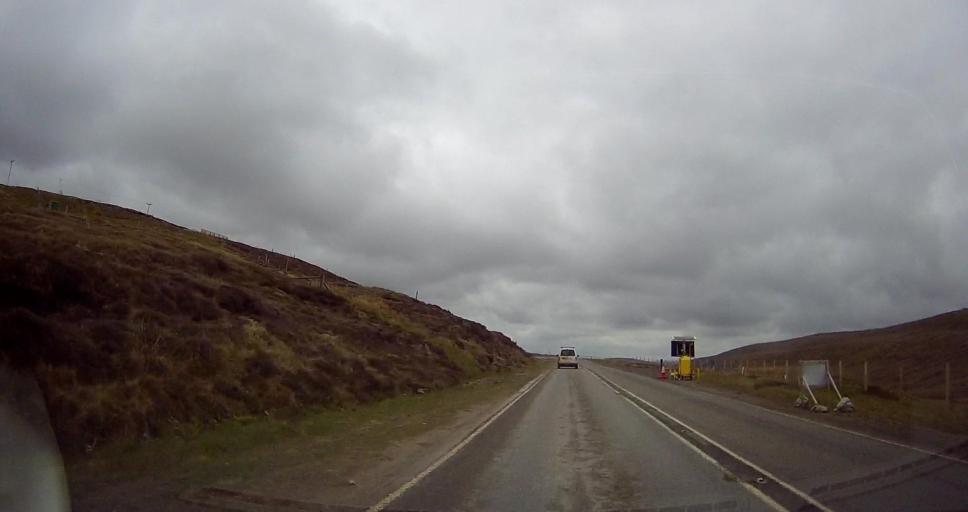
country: GB
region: Scotland
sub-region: Shetland Islands
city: Lerwick
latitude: 60.3246
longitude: -1.2524
